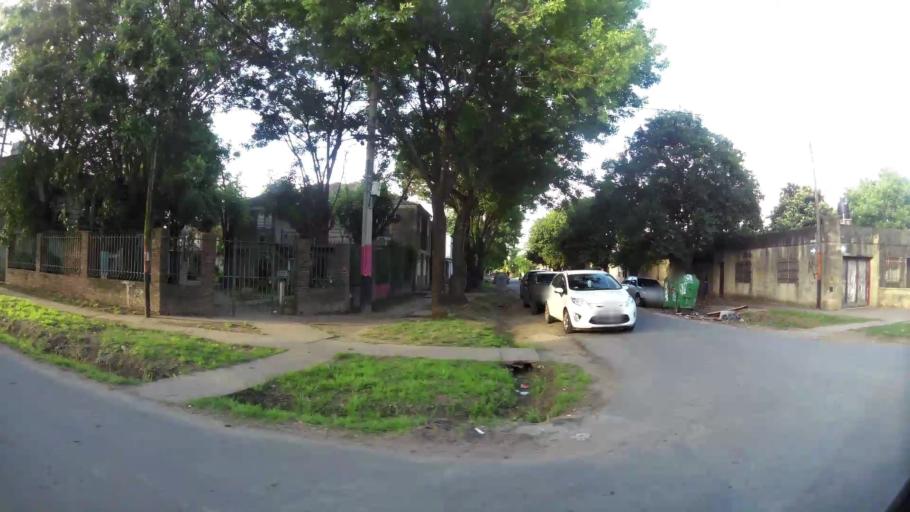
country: AR
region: Santa Fe
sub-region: Departamento de Rosario
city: Rosario
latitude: -32.9828
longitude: -60.6660
